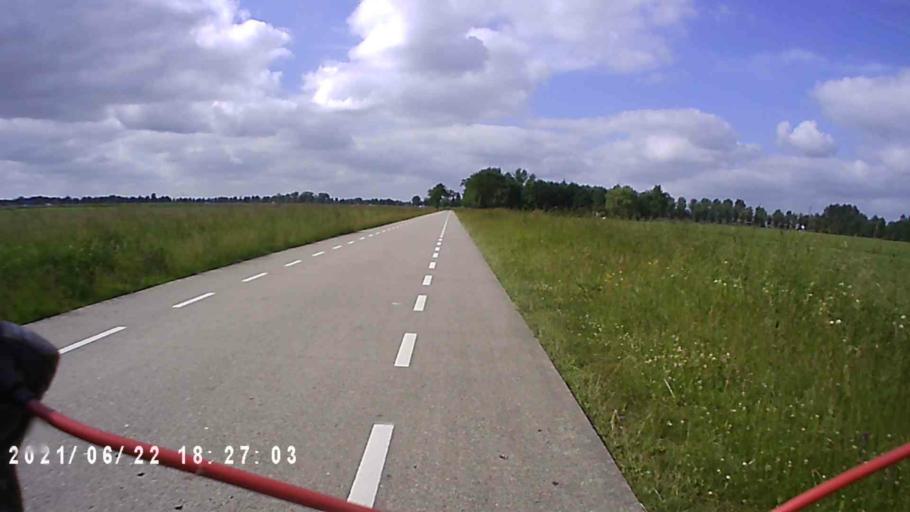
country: NL
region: Groningen
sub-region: Gemeente Zuidhorn
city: Aduard
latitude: 53.1965
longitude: 6.4620
